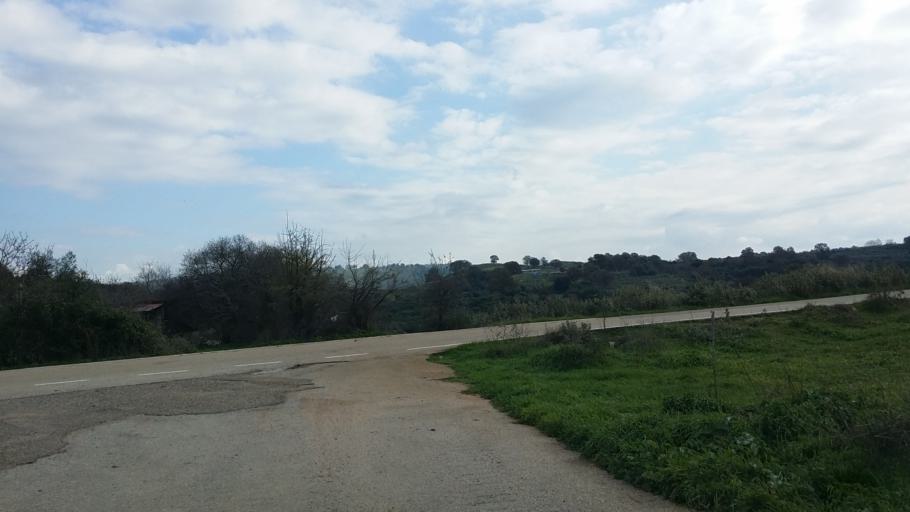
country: GR
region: West Greece
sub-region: Nomos Aitolias kai Akarnanias
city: Katouna
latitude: 38.8581
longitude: 21.0693
